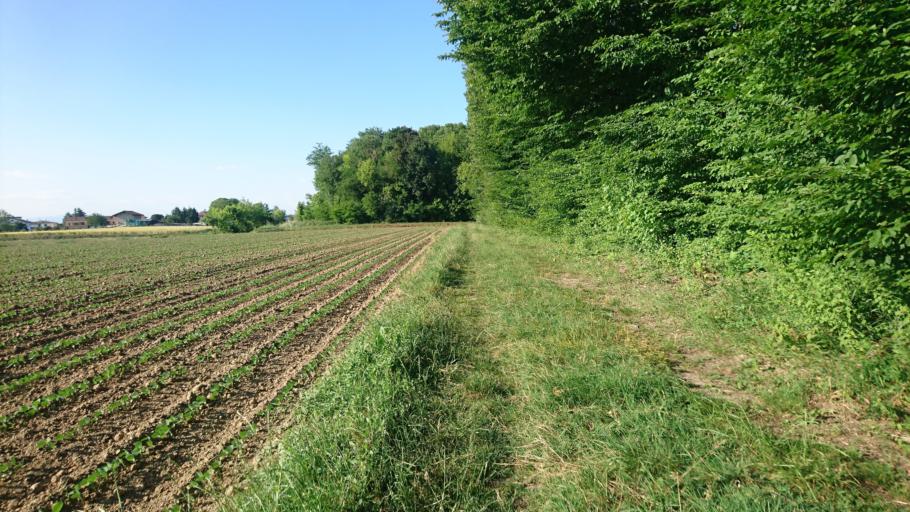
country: IT
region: Veneto
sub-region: Provincia di Padova
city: Ponte San Nicolo
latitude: 45.3627
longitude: 11.9234
